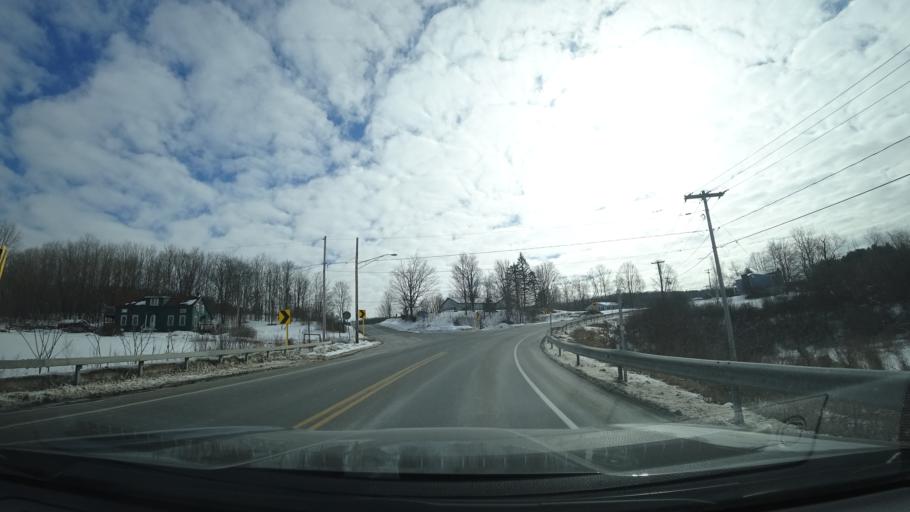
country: US
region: New York
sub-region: Washington County
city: Fort Edward
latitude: 43.2567
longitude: -73.5060
